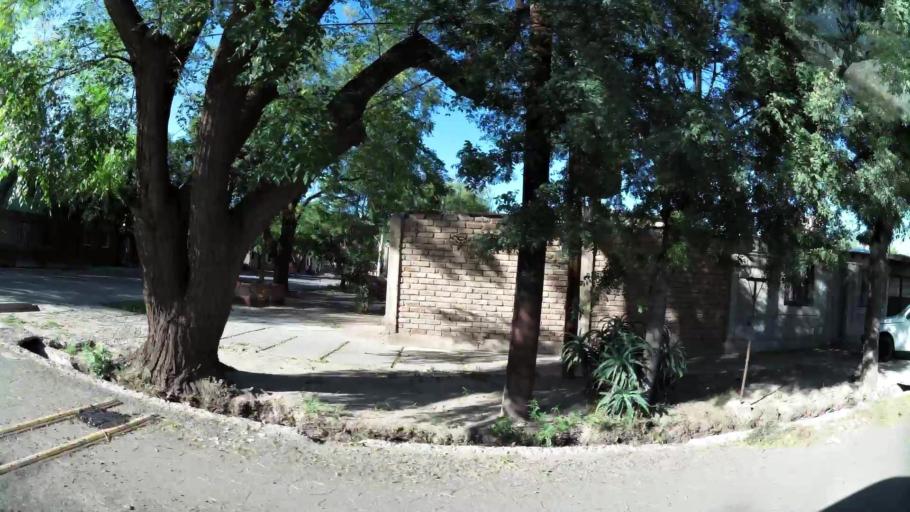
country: AR
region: Mendoza
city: Las Heras
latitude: -32.8577
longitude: -68.8171
